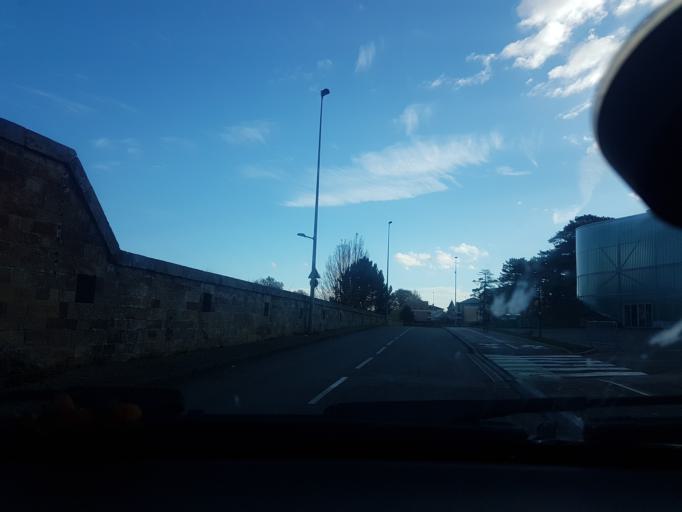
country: FR
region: Franche-Comte
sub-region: Territoire de Belfort
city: Belfort
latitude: 47.6396
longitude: 6.8501
